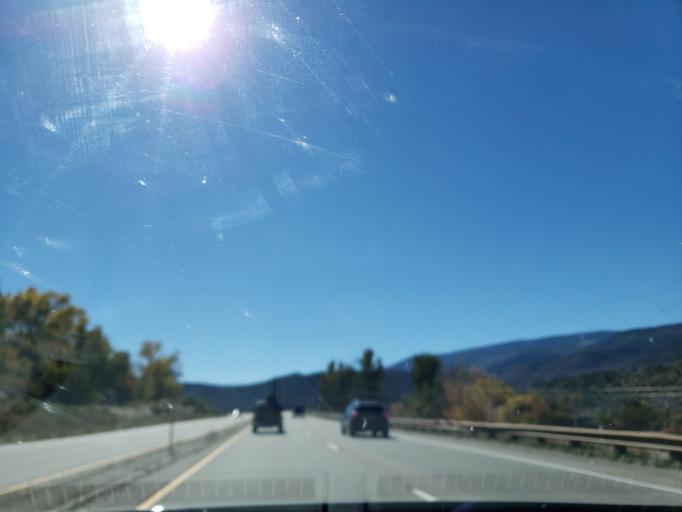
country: US
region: Colorado
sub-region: Garfield County
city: Glenwood Springs
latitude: 39.5020
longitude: -107.3017
